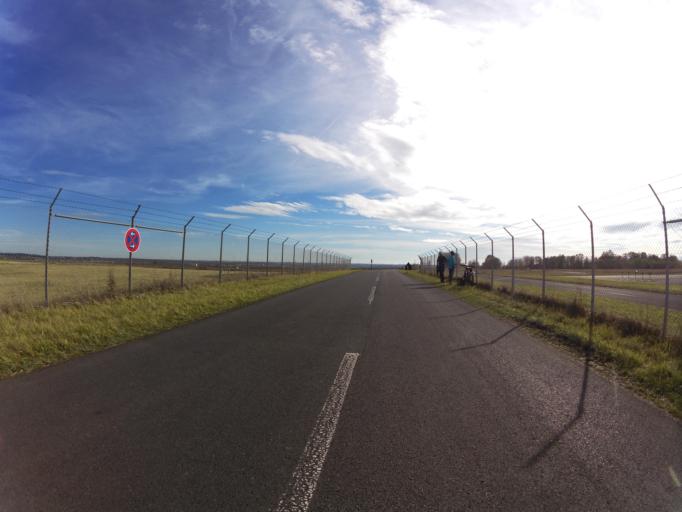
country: DE
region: Bavaria
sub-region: Regierungsbezirk Unterfranken
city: Gaukonigshofen
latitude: 49.6504
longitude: 9.9814
